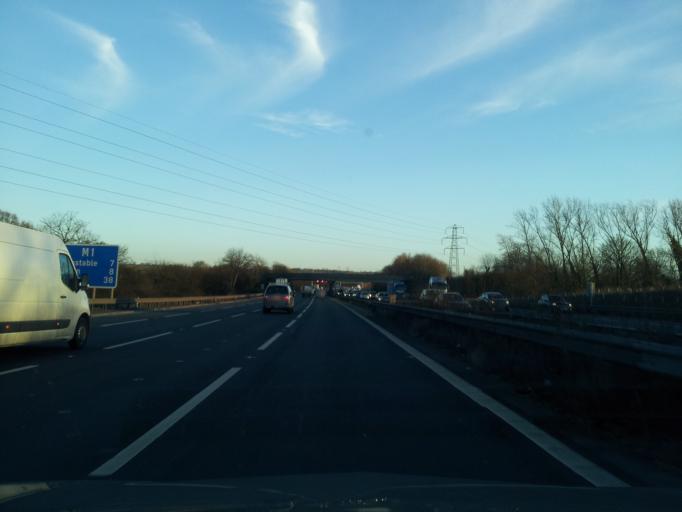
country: GB
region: England
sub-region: Central Bedfordshire
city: Toddington
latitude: 51.9554
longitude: -0.5129
